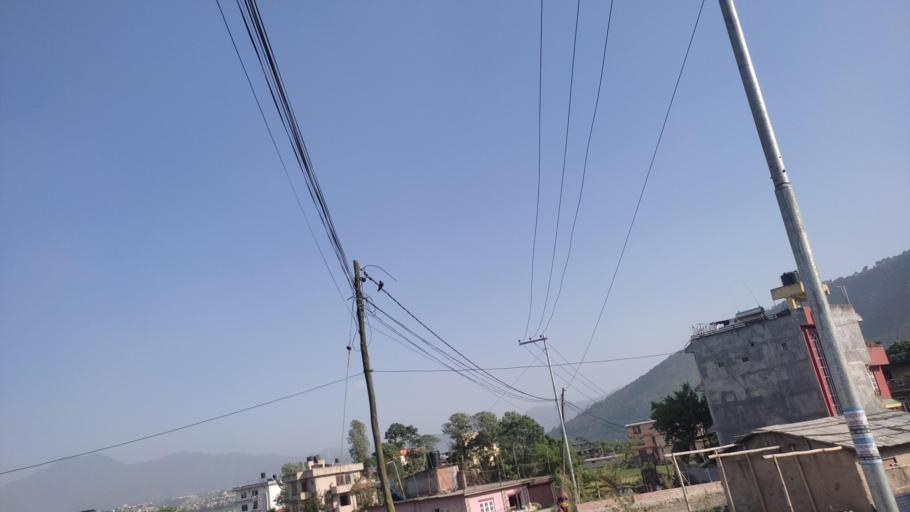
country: NP
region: Central Region
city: Kirtipur
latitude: 27.6543
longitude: 85.2796
